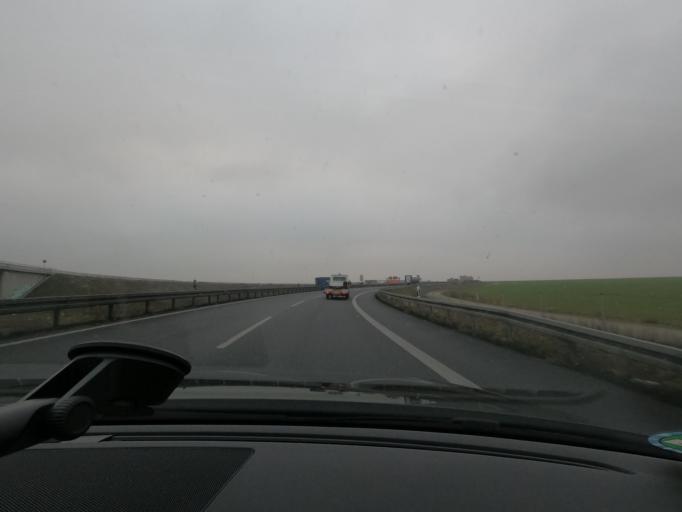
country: DE
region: North Rhine-Westphalia
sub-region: Regierungsbezirk Dusseldorf
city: Juchen
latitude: 51.0903
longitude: 6.4759
